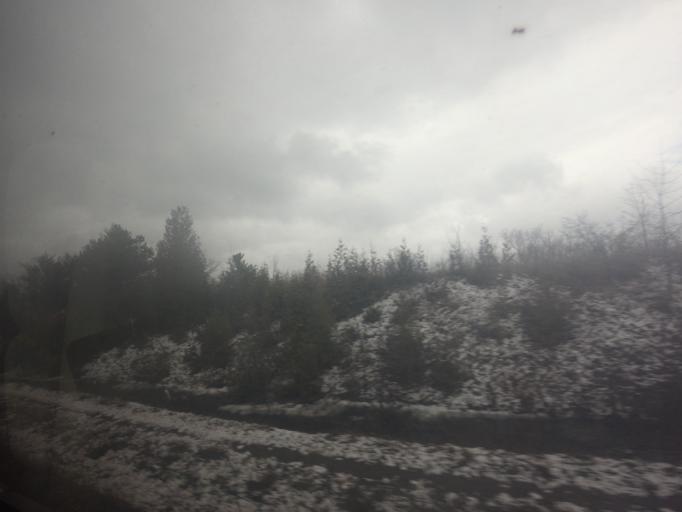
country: CA
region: Ontario
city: Cobourg
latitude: 43.9410
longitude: -78.3130
